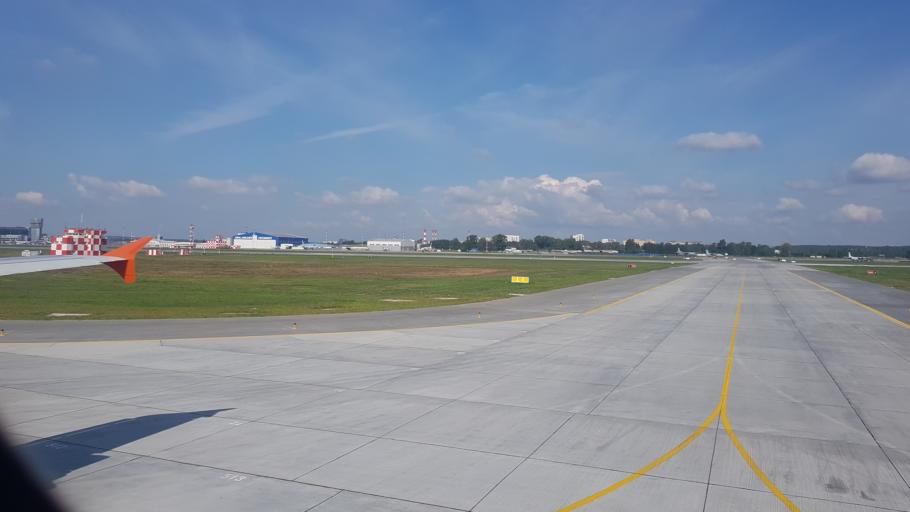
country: RU
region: Sverdlovsk
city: Aramil
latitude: 56.7408
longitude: 60.8214
